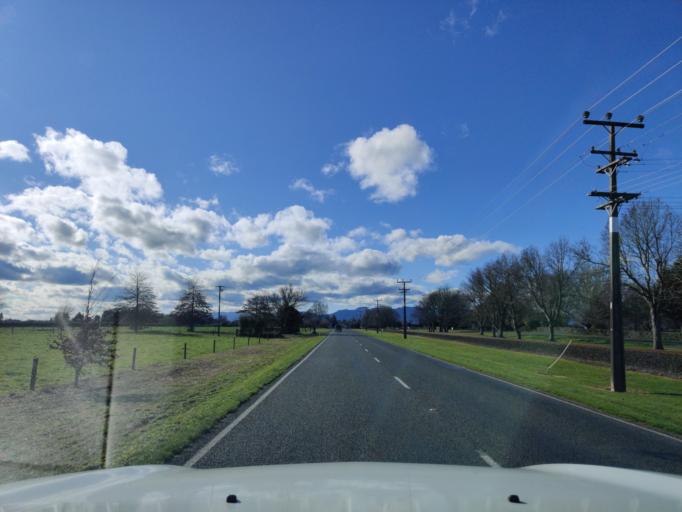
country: NZ
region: Waikato
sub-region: Matamata-Piako District
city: Matamata
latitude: -37.8327
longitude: 175.7668
